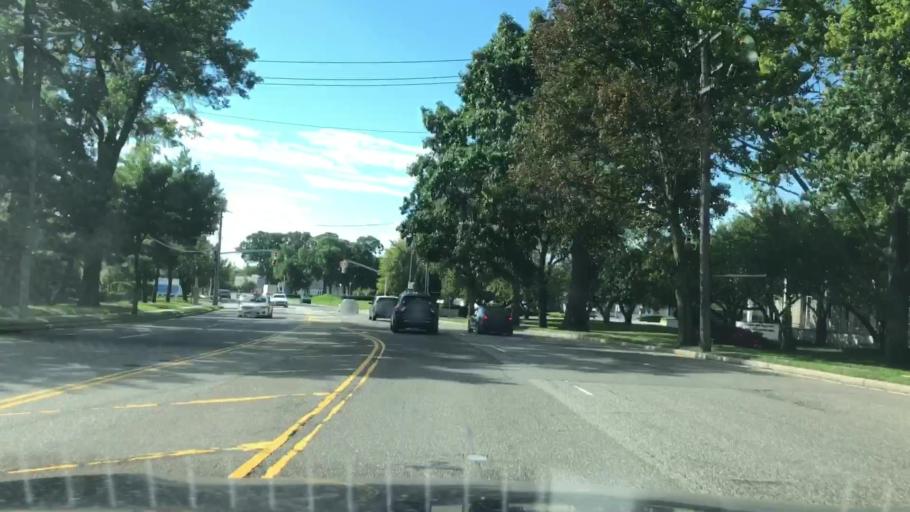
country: US
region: New York
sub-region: Nassau County
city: Lake Success
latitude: 40.7583
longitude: -73.7045
